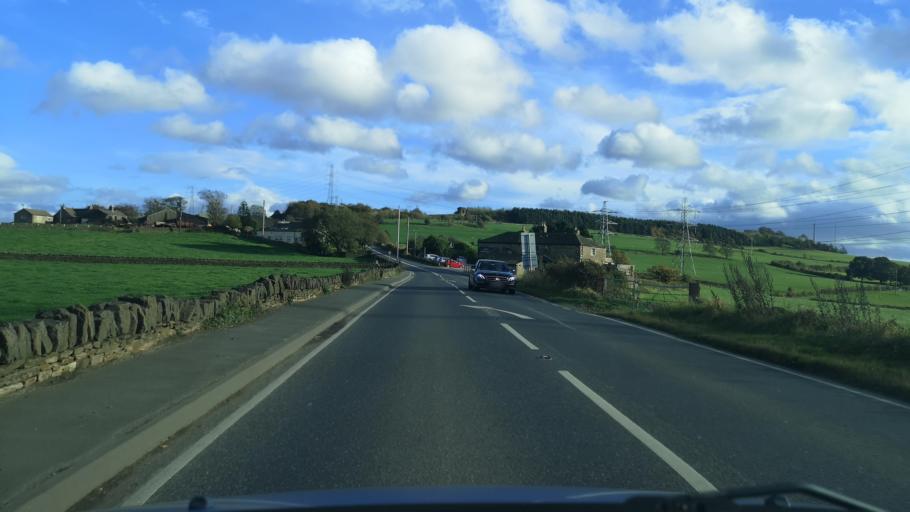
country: GB
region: England
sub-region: Kirklees
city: Mirfield
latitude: 53.6527
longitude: -1.6940
